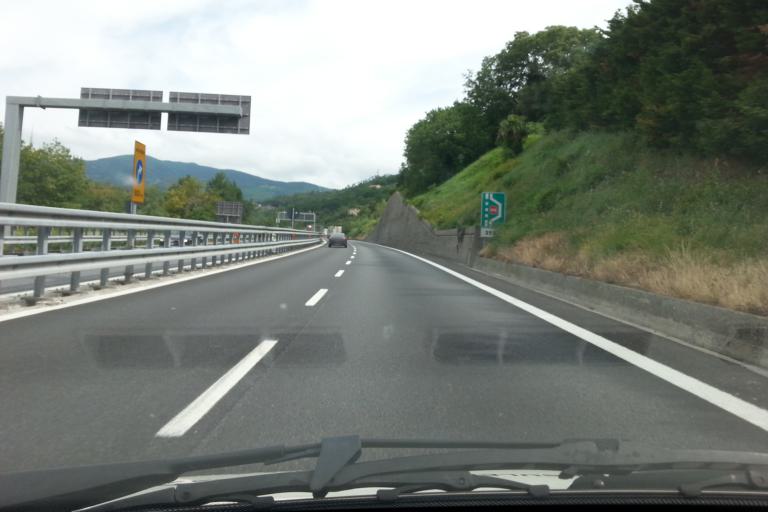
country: IT
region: Liguria
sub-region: Provincia di Savona
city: Calice Ligure
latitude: 44.1911
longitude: 8.3064
